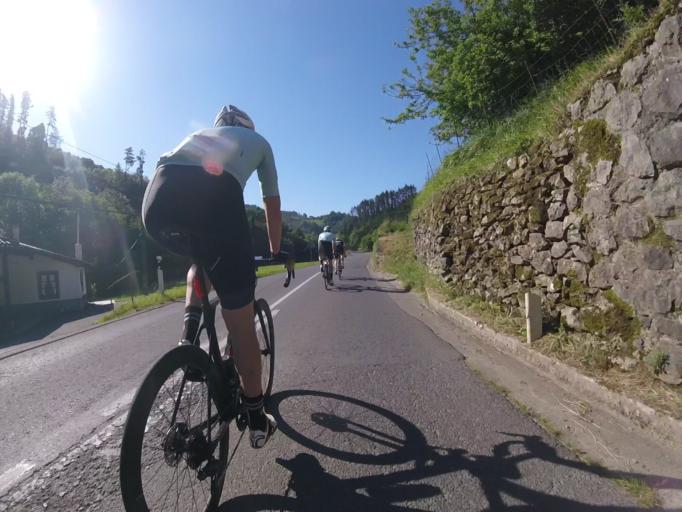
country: ES
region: Basque Country
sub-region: Provincia de Guipuzcoa
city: Beizama
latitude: 43.1502
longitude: -2.2377
